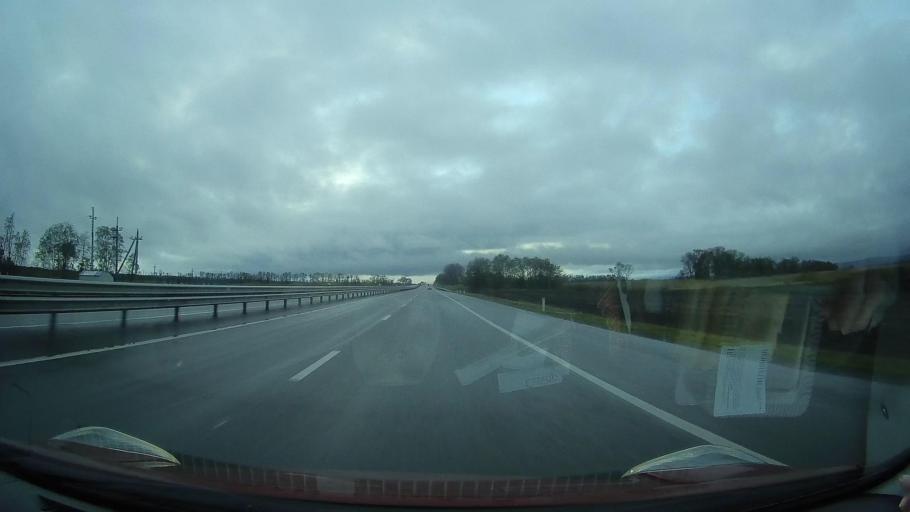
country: RU
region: Stavropol'skiy
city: Zavetnoye
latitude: 44.7855
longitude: 41.5176
